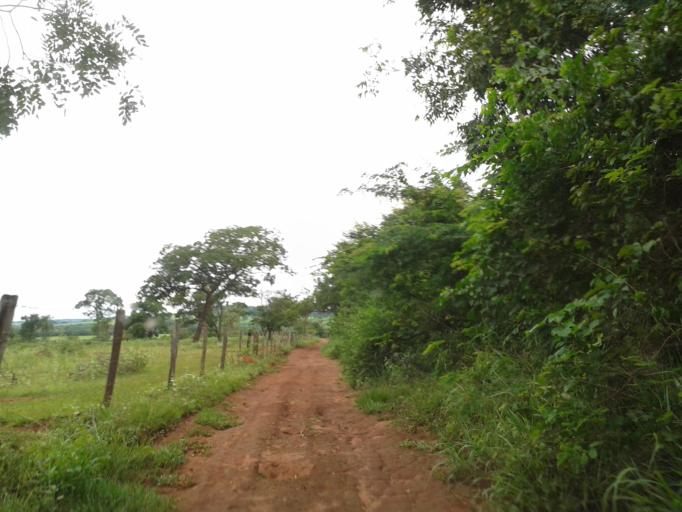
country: BR
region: Minas Gerais
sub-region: Santa Vitoria
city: Santa Vitoria
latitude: -18.7950
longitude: -49.8507
